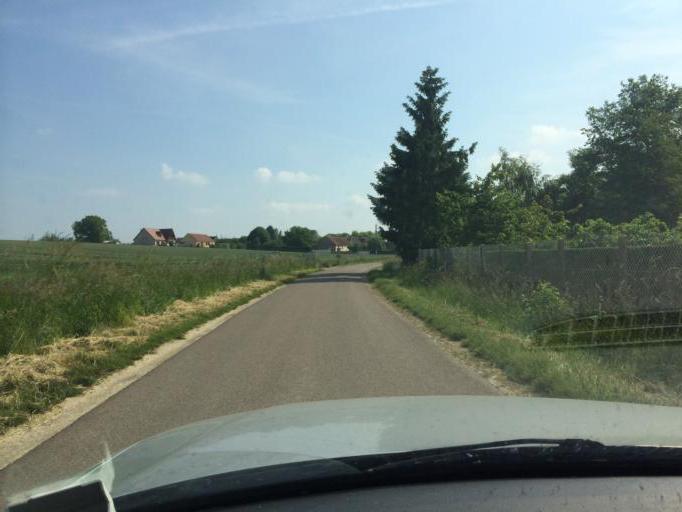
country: FR
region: Bourgogne
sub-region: Departement de l'Yonne
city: Fleury-la-Vallee
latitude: 47.8790
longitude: 3.4059
